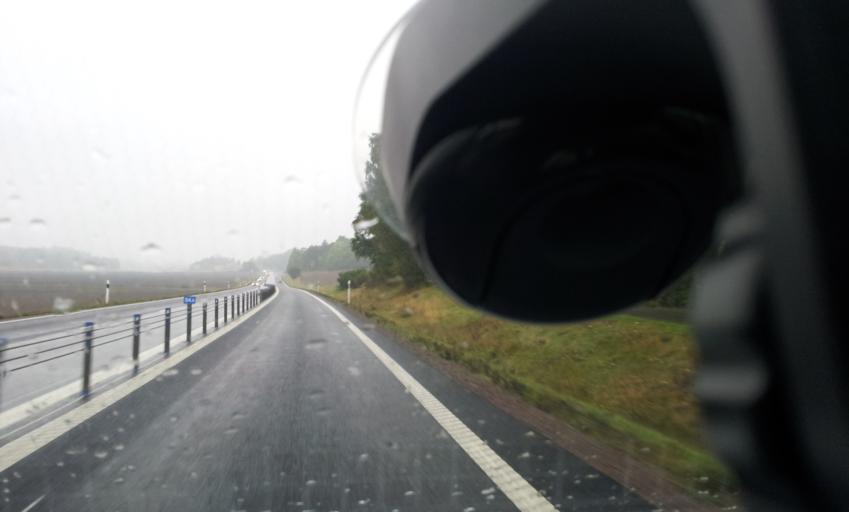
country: SE
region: OEstergoetland
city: Lindo
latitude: 58.5460
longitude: 16.2645
